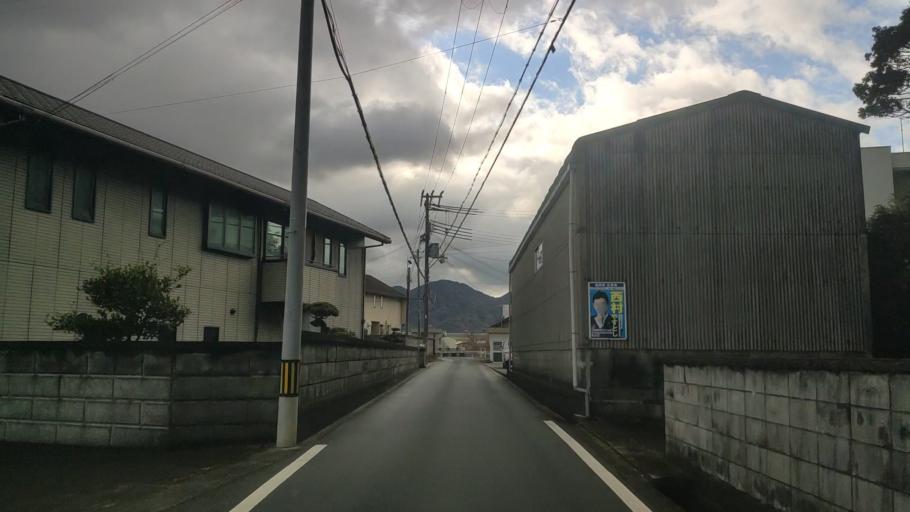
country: JP
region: Hyogo
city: Sumoto
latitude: 34.3278
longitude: 134.8534
